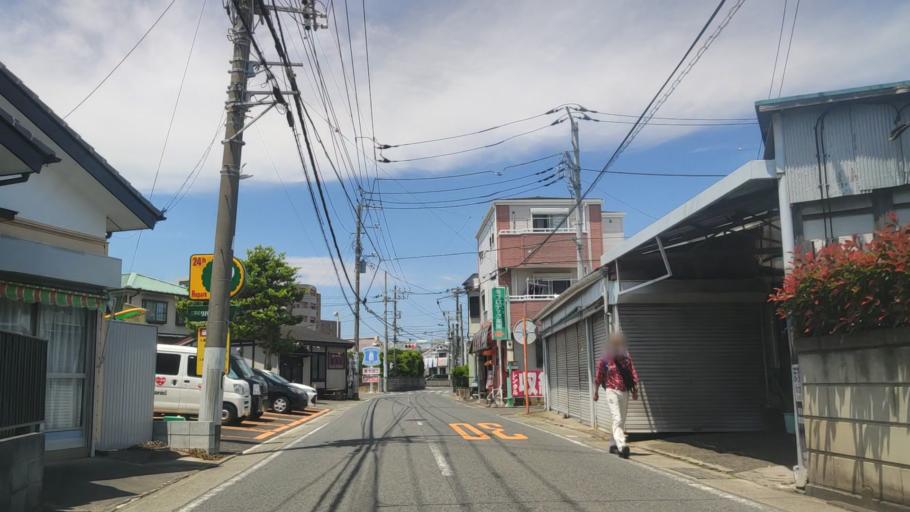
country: JP
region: Kanagawa
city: Chigasaki
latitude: 35.3386
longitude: 139.3977
